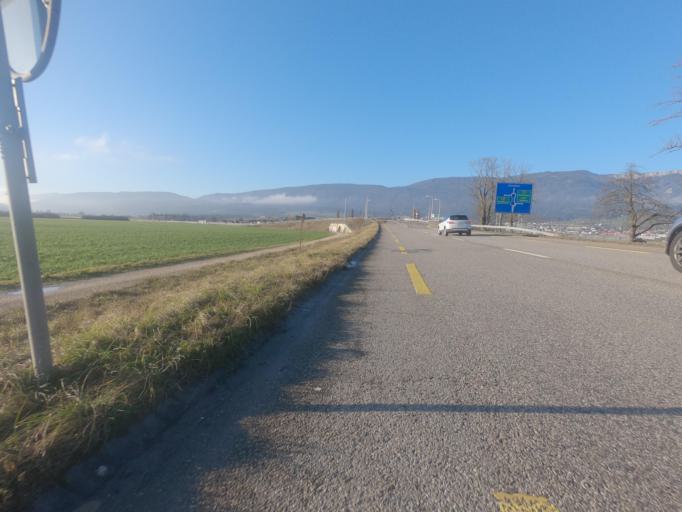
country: CH
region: Bern
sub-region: Seeland District
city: Arch
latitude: 47.1736
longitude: 7.4192
